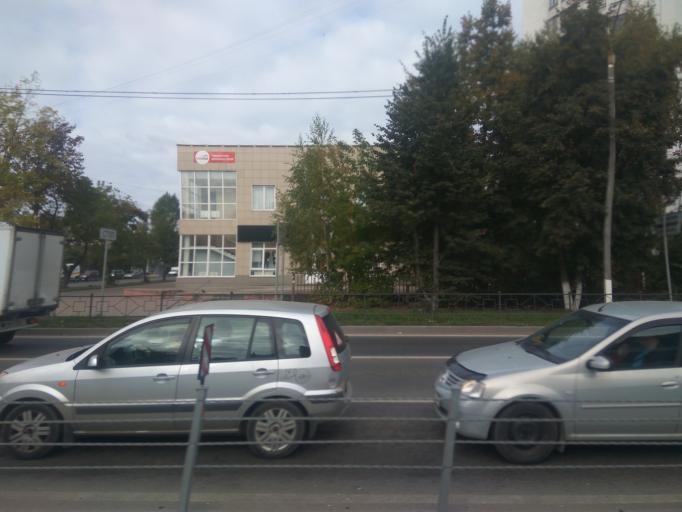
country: RU
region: Moskovskaya
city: Fryazino
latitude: 55.9522
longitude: 38.0519
